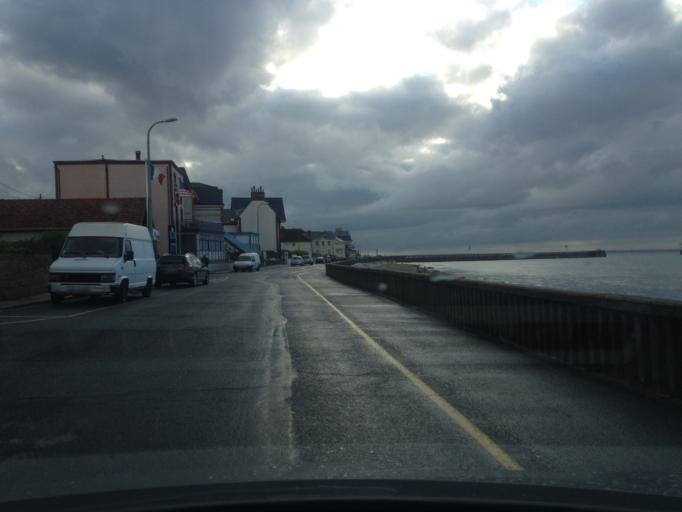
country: FR
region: Lower Normandy
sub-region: Departement du Calvados
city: Grandcamp-Maisy
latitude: 49.3891
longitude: -1.0425
